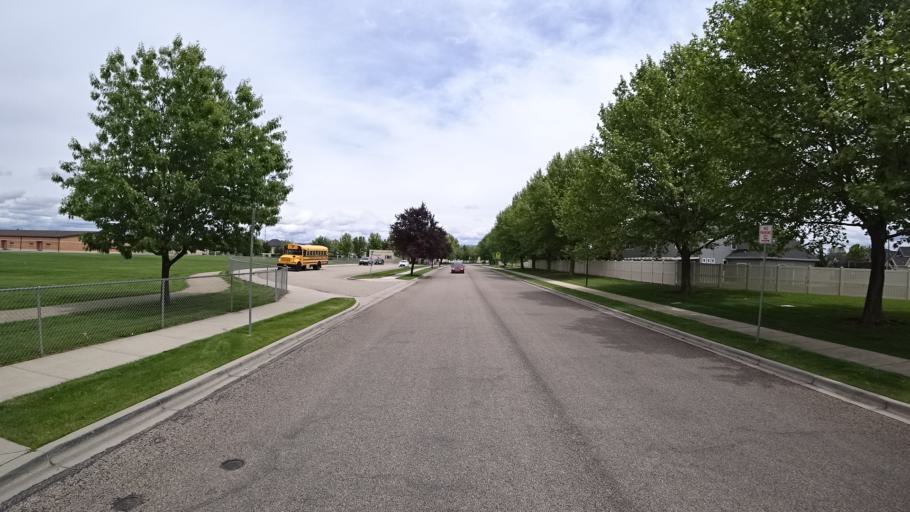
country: US
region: Idaho
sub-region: Ada County
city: Meridian
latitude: 43.6457
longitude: -116.4208
